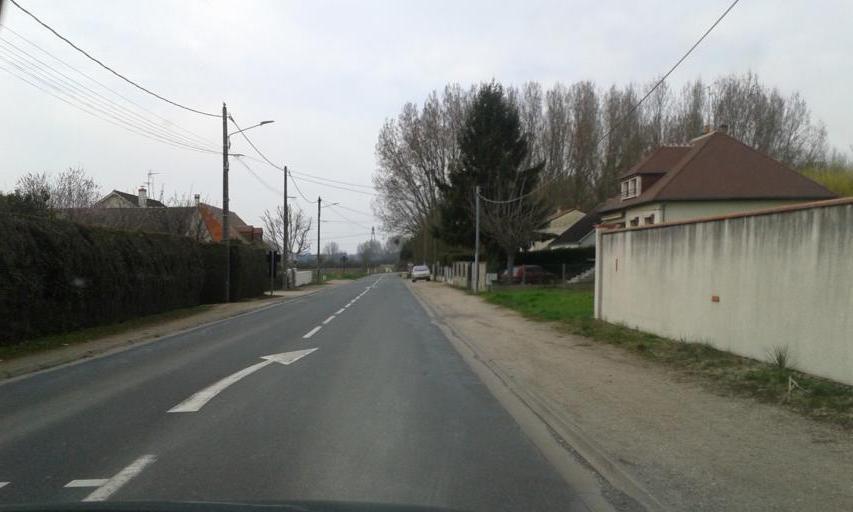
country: FR
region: Centre
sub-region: Departement du Loiret
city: Clery-Saint-Andre
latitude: 47.8224
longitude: 1.7508
